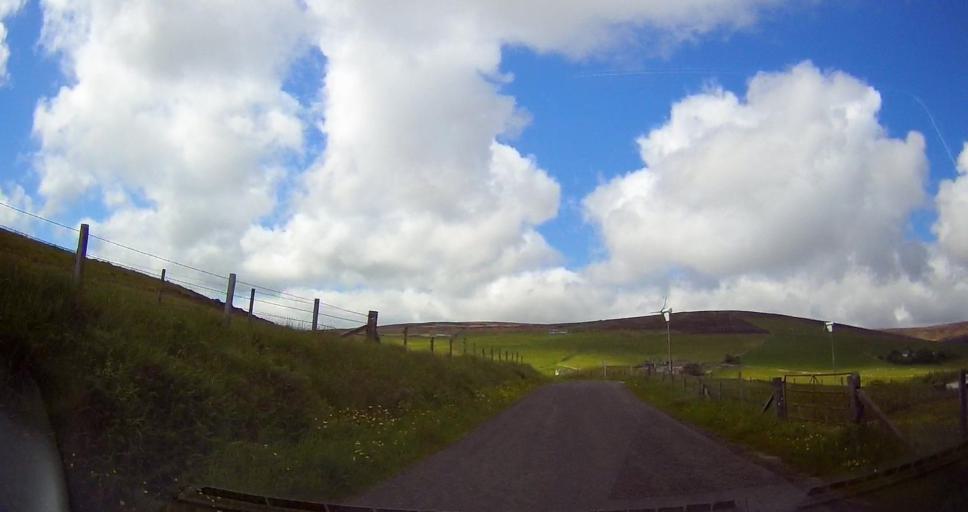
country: GB
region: Scotland
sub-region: Orkney Islands
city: Orkney
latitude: 59.0495
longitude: -3.1029
